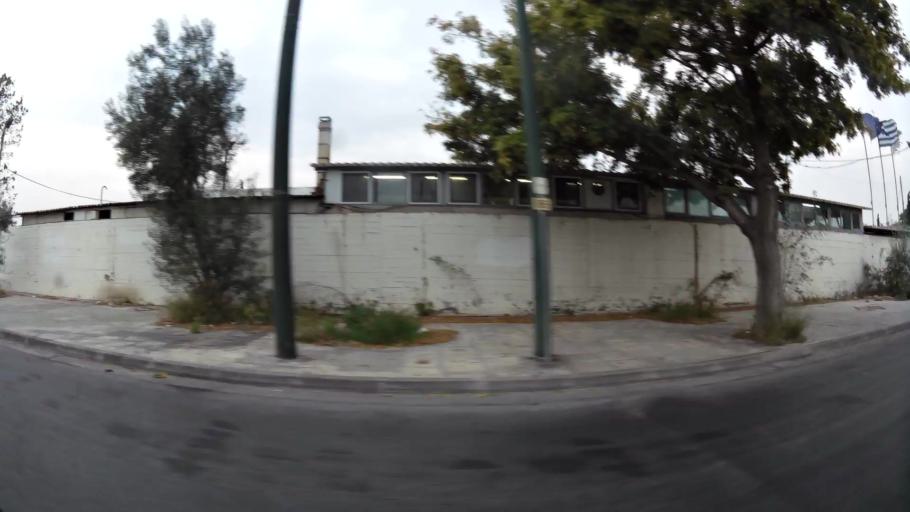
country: GR
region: Attica
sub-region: Nomarchia Athinas
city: Tavros
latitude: 37.9761
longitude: 23.6906
